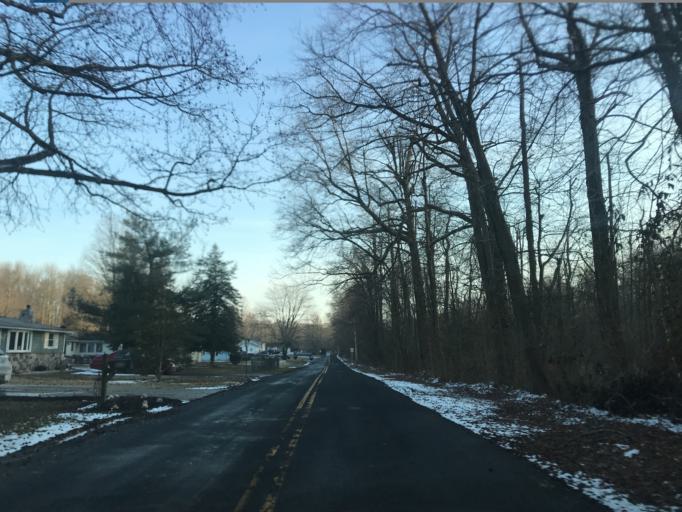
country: US
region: Maryland
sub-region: Harford County
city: Riverside
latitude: 39.4381
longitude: -76.2566
